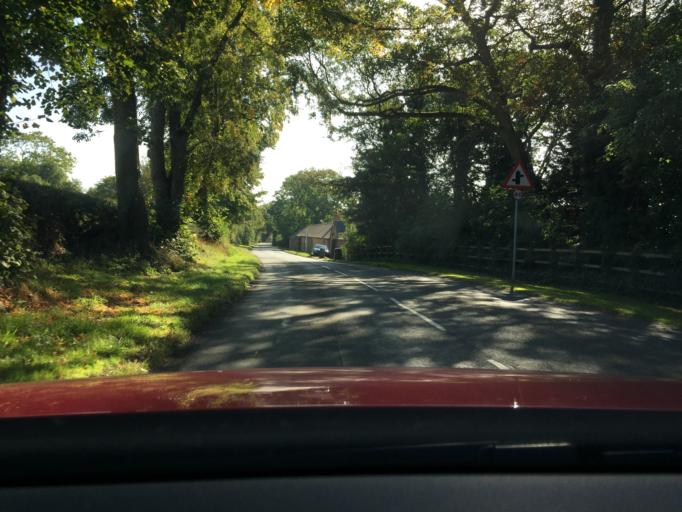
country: GB
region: England
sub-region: Leicestershire
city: Houghton on the Hill
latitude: 52.6533
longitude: -1.0105
